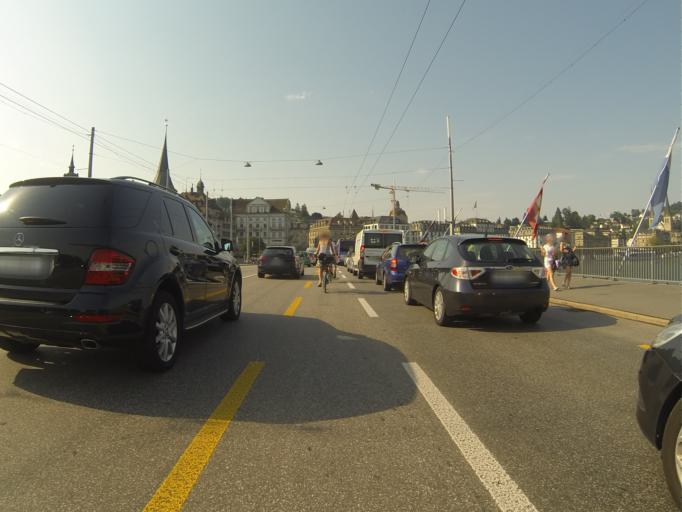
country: CH
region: Lucerne
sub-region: Lucerne-Stadt District
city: Luzern
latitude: 47.0517
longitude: 8.3091
